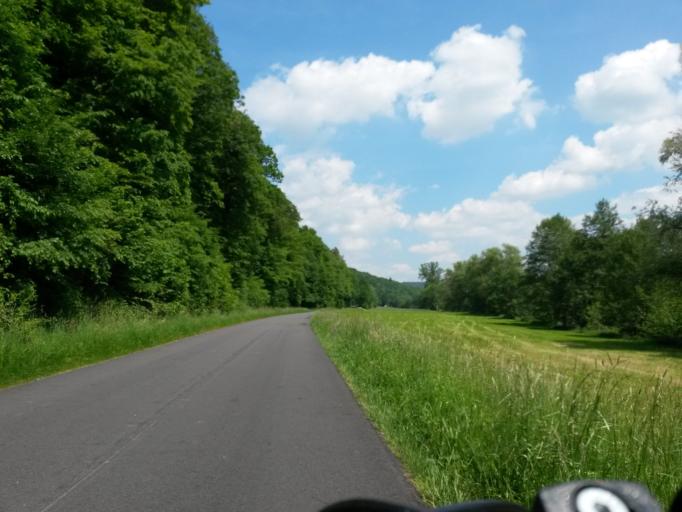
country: DE
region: Bavaria
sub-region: Regierungsbezirk Unterfranken
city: Elfershausen
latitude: 50.1568
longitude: 9.9907
